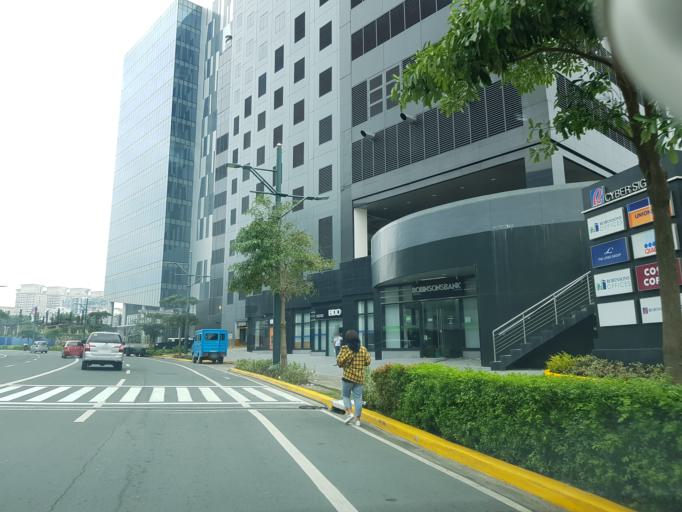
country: PH
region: Metro Manila
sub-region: Makati City
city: Makati City
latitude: 14.5358
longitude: 121.0429
